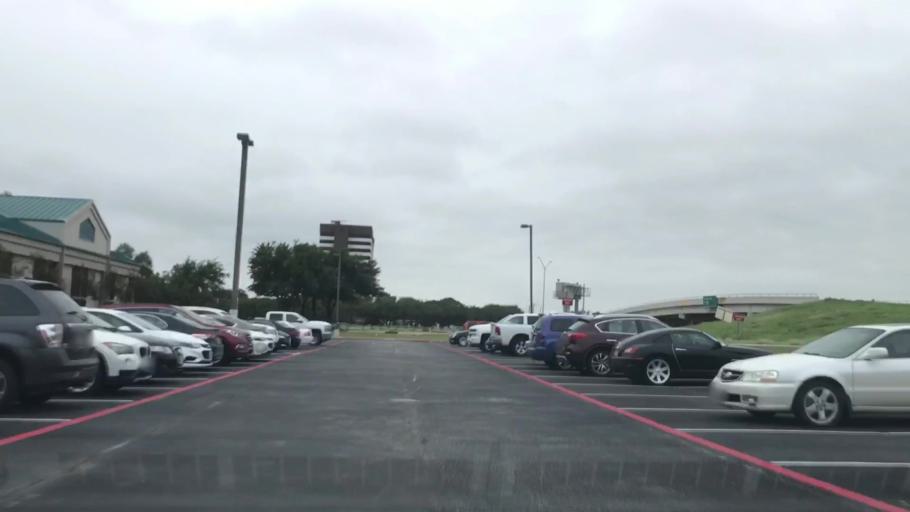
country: US
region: Texas
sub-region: Dallas County
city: Coppell
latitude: 32.9166
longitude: -97.0073
